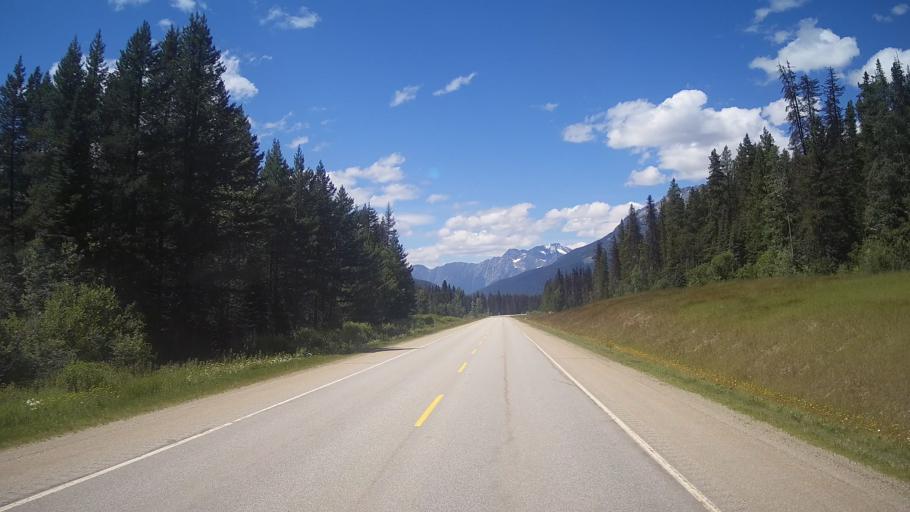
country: CA
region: Alberta
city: Grande Cache
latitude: 52.9884
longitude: -119.0037
